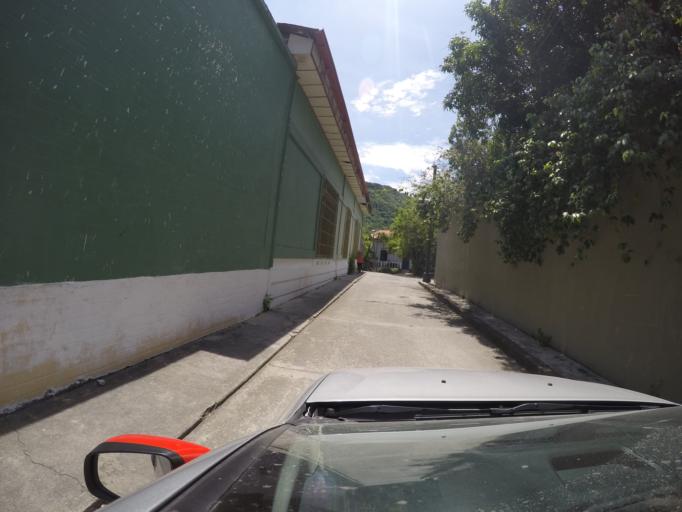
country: CO
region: Tolima
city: Honda
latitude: 5.2022
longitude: -74.7368
